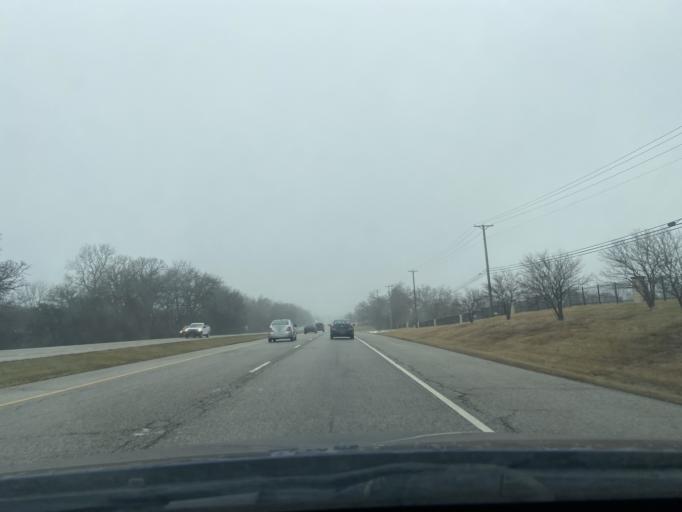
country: US
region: Illinois
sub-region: Lake County
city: Knollwood
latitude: 42.2216
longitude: -88.1114
